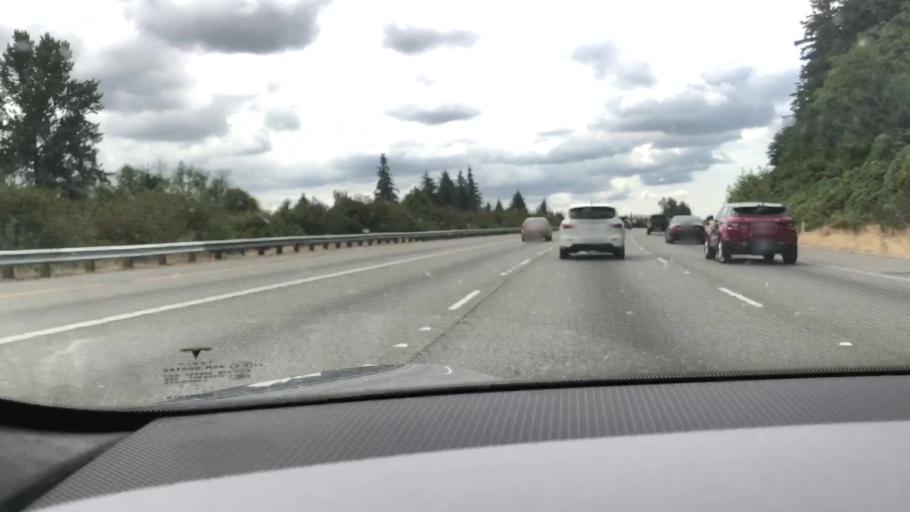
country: US
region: Washington
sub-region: Snohomish County
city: Martha Lake
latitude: 47.8644
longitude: -122.2471
